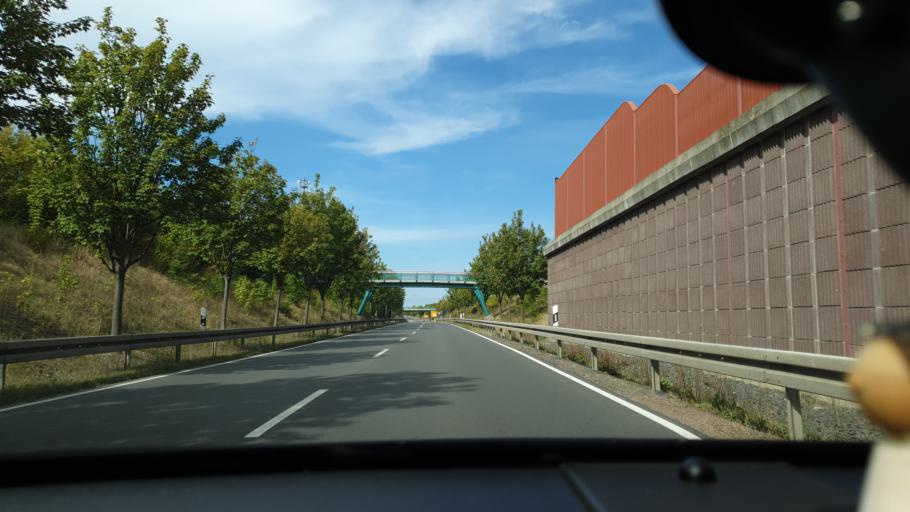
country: DE
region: Saxony
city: Eilenburg
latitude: 51.4551
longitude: 12.6119
